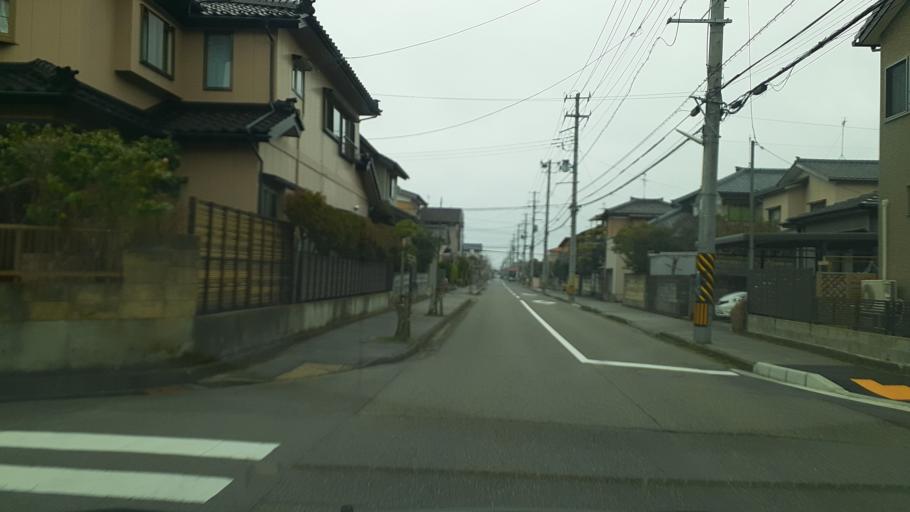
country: JP
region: Niigata
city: Niigata-shi
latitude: 37.8647
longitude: 139.0417
